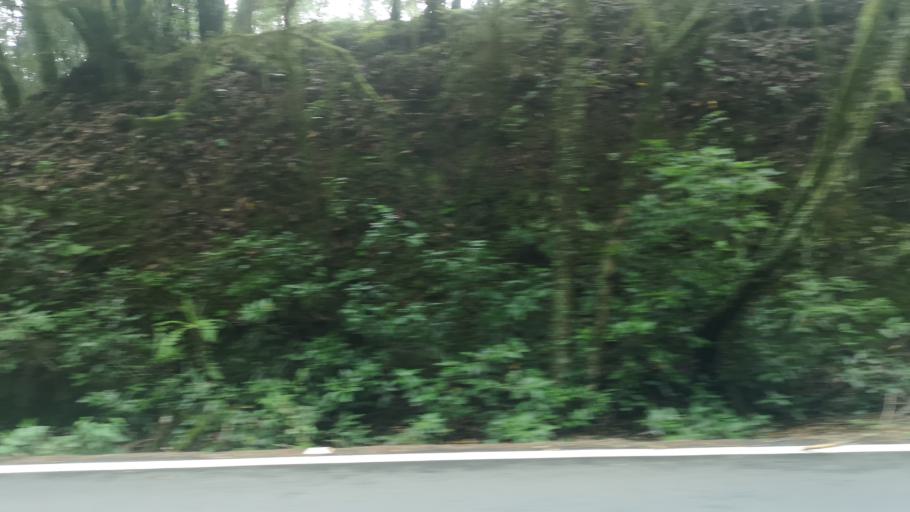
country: ES
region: Canary Islands
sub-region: Provincia de Santa Cruz de Tenerife
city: Alajero
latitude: 28.1114
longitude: -17.2186
